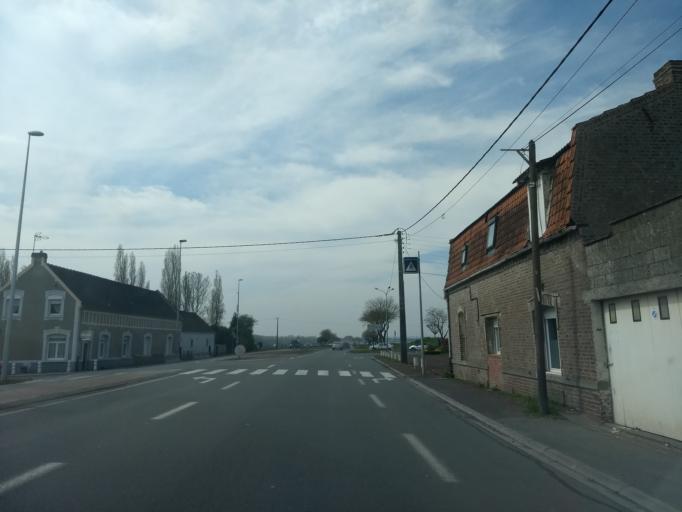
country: FR
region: Nord-Pas-de-Calais
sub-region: Departement du Pas-de-Calais
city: Vitry-en-Artois
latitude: 50.3325
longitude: 2.9741
